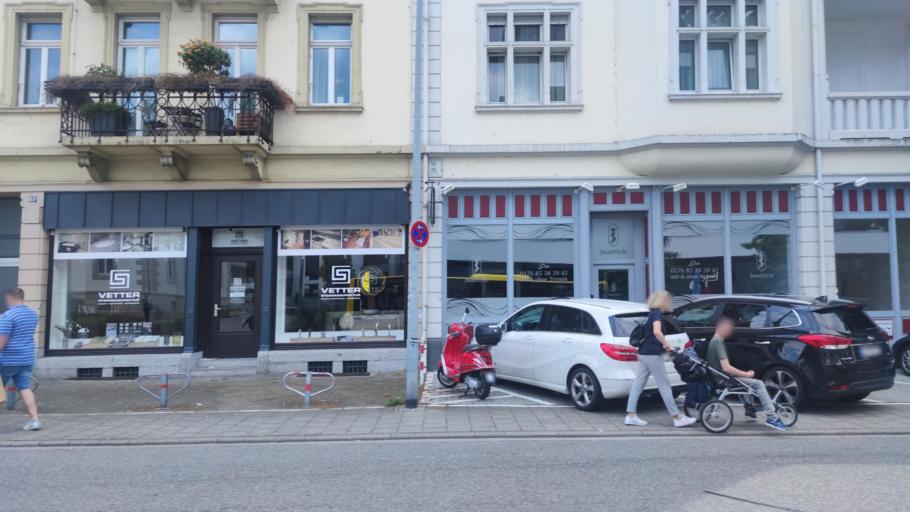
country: DE
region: Baden-Wuerttemberg
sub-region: Karlsruhe Region
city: Baden-Baden
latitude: 48.7685
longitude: 8.2314
